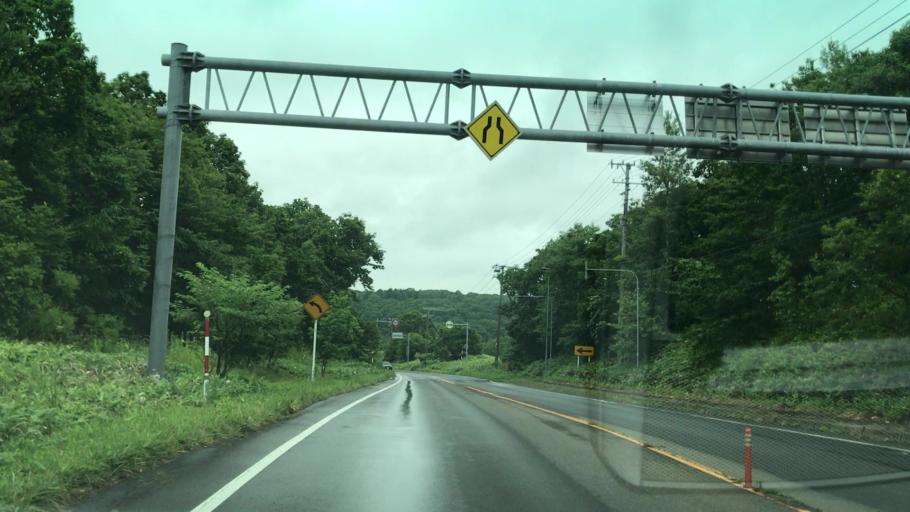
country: JP
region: Hokkaido
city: Muroran
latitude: 42.3841
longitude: 140.9644
